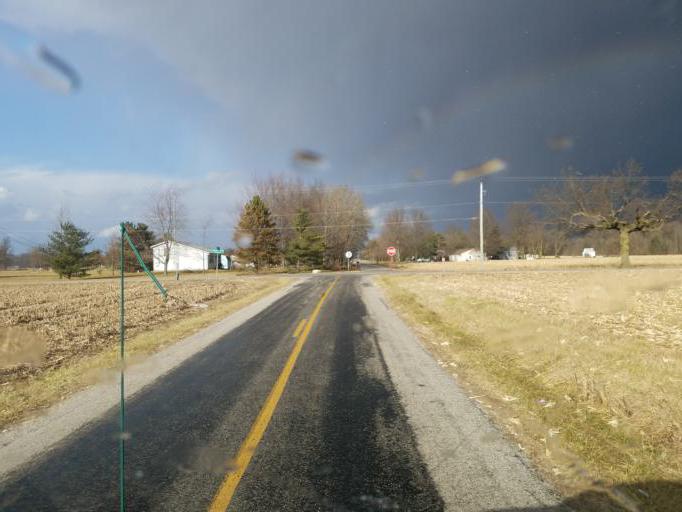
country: US
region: Ohio
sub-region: Marion County
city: Prospect
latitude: 40.4832
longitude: -83.1179
